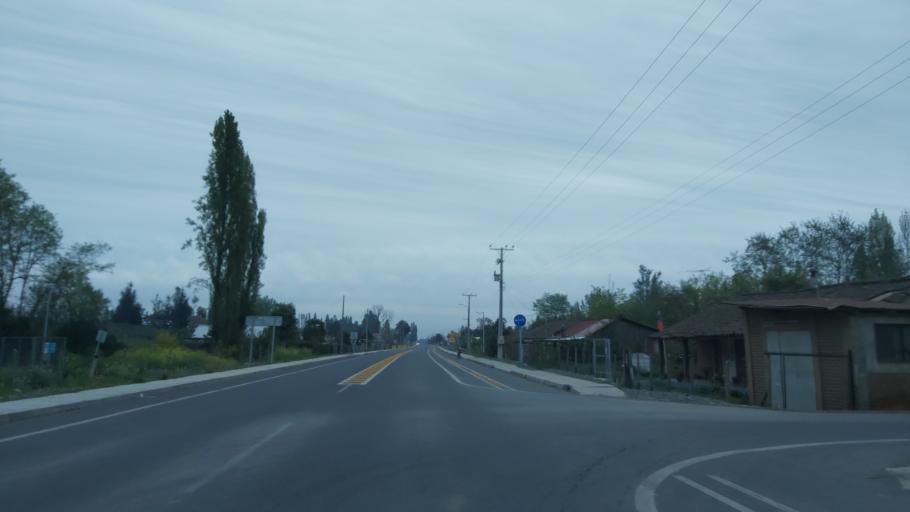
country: CL
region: Maule
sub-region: Provincia de Linares
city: Colbun
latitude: -35.6704
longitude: -71.4630
